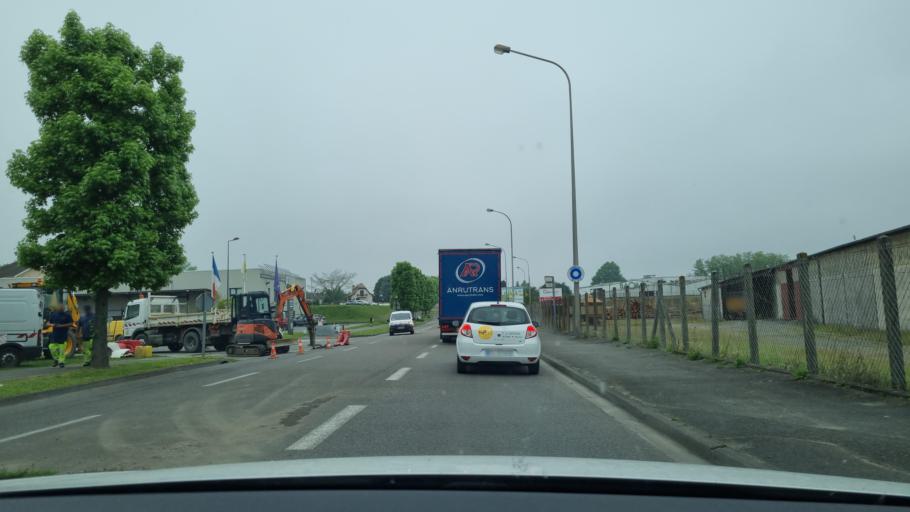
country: FR
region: Aquitaine
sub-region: Departement des Pyrenees-Atlantiques
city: Orthez
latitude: 43.4782
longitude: -0.7628
